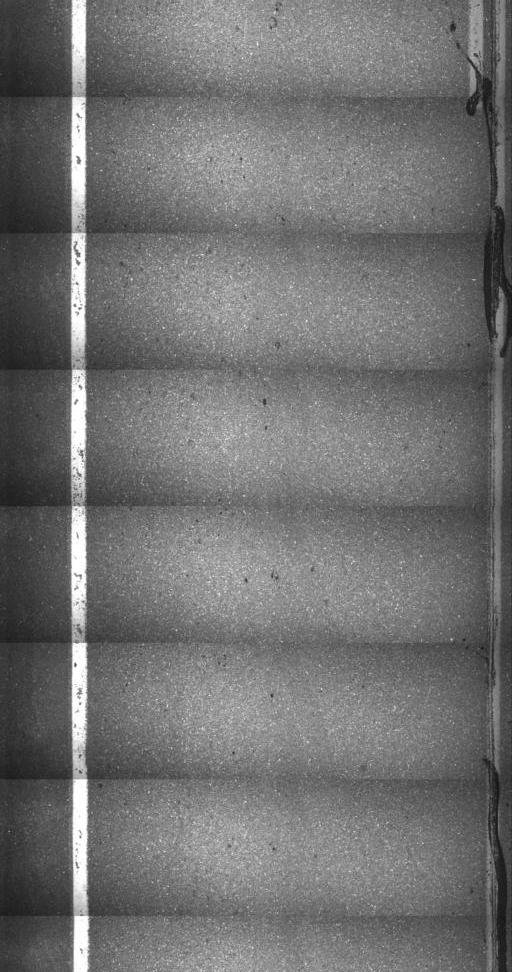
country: US
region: Vermont
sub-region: Orleans County
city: Newport
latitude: 44.9748
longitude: -72.3245
